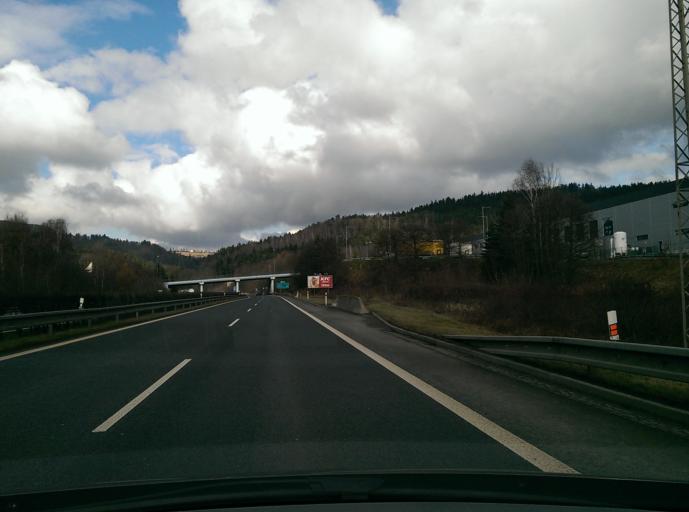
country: CZ
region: Liberecky
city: Hodkovice nad Mohelkou
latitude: 50.6646
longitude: 15.0963
